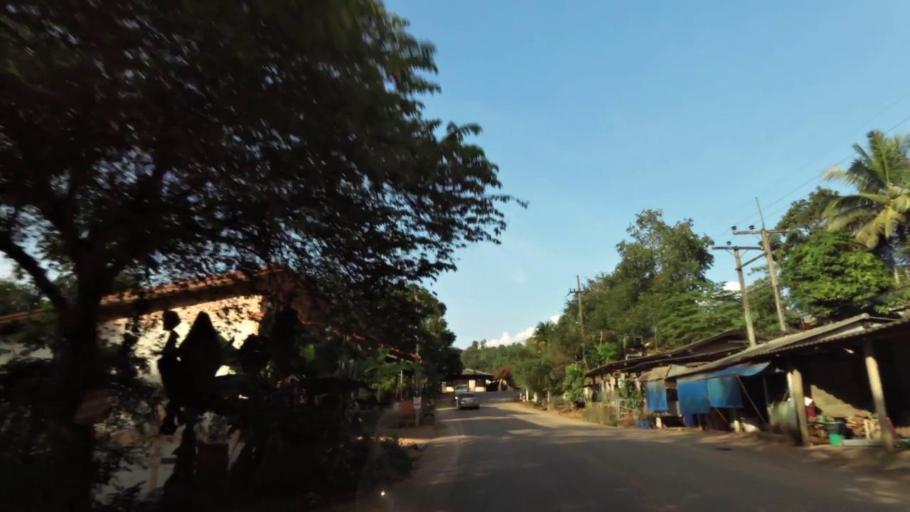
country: TH
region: Chiang Rai
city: Khun Tan
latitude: 19.8665
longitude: 100.3991
